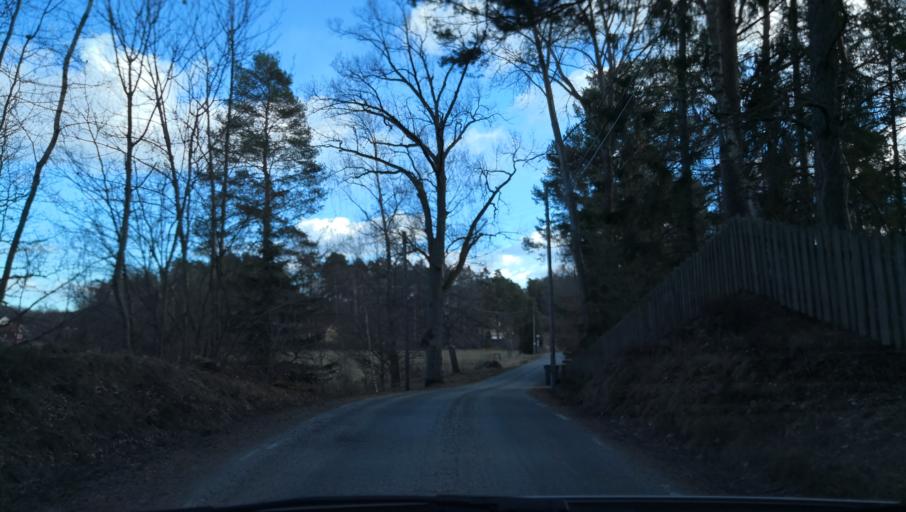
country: SE
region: Stockholm
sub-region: Varmdo Kommun
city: Mortnas
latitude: 59.3834
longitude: 18.4549
